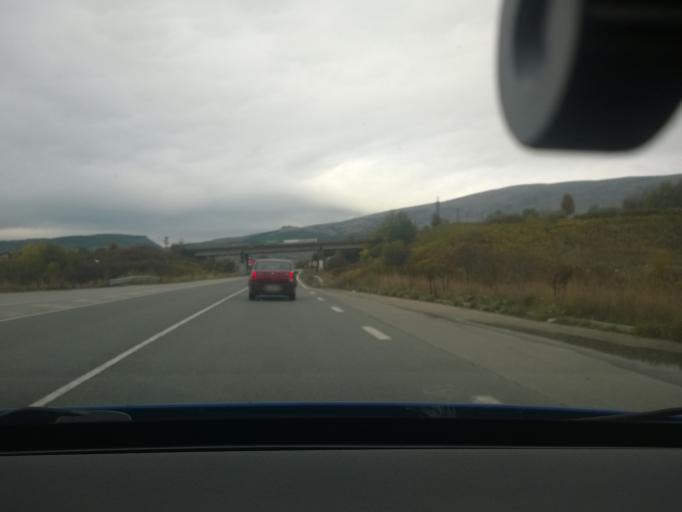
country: BG
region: Sofiya
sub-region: Obshtina Dragoman
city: Dragoman
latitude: 42.9229
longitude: 22.9368
